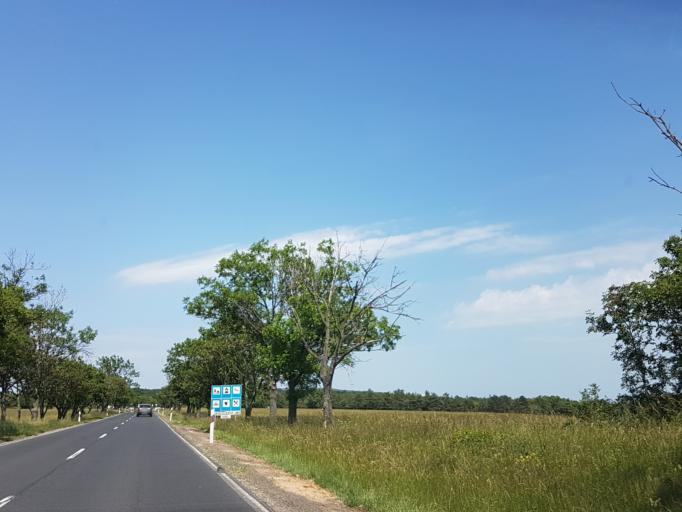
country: HU
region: Veszprem
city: Zanka
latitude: 46.8780
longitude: 17.6909
